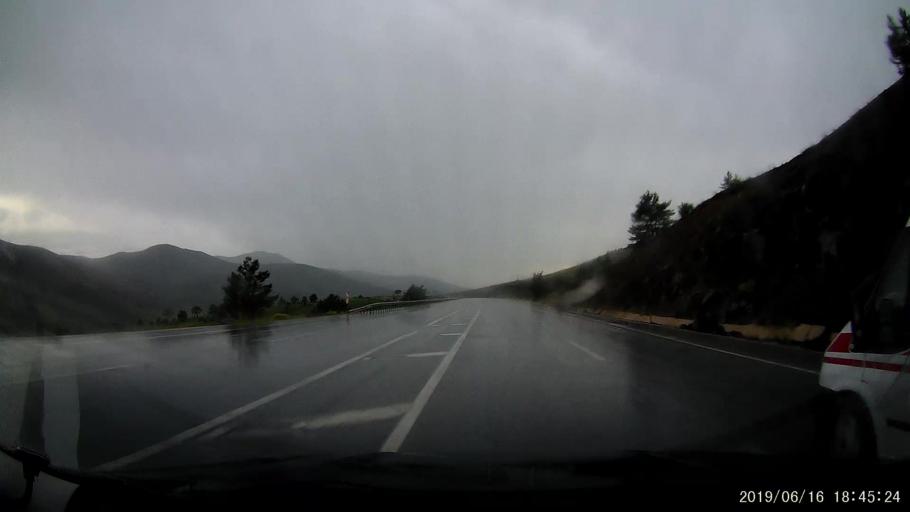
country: TR
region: Erzincan
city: Doganbeyli
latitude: 39.8704
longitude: 39.0575
